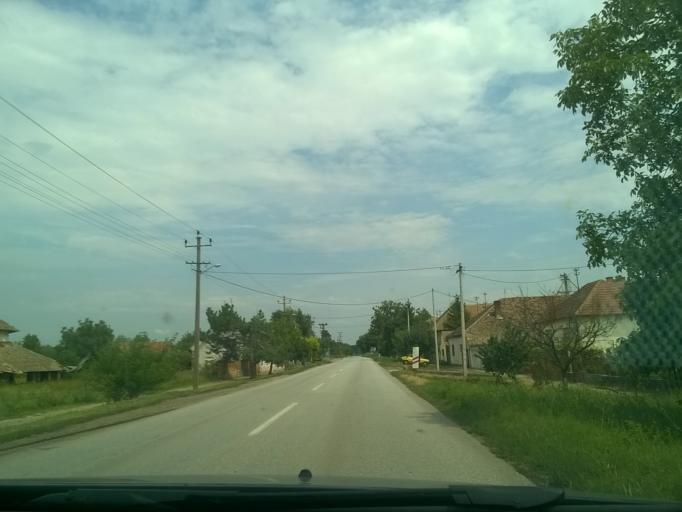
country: RS
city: Velika Greda
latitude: 45.2447
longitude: 21.0467
